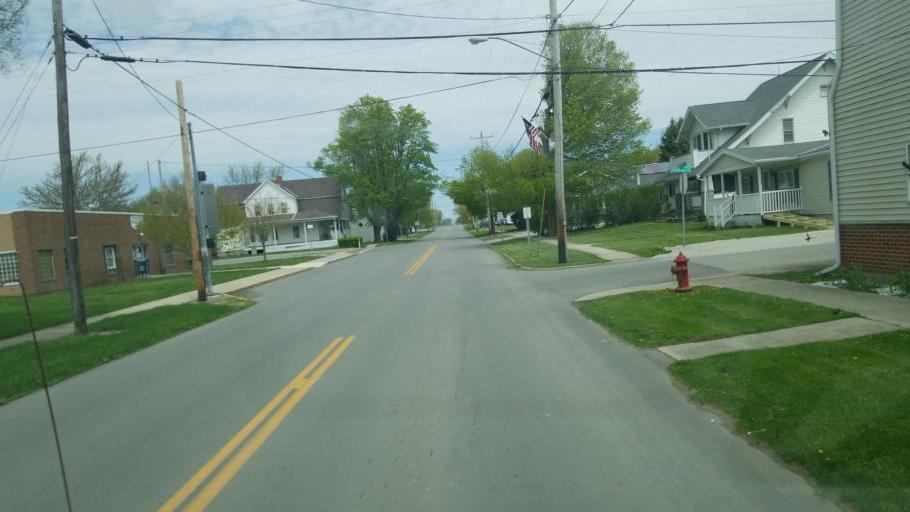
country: US
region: Ohio
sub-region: Hardin County
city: Ada
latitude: 40.6923
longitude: -83.7853
